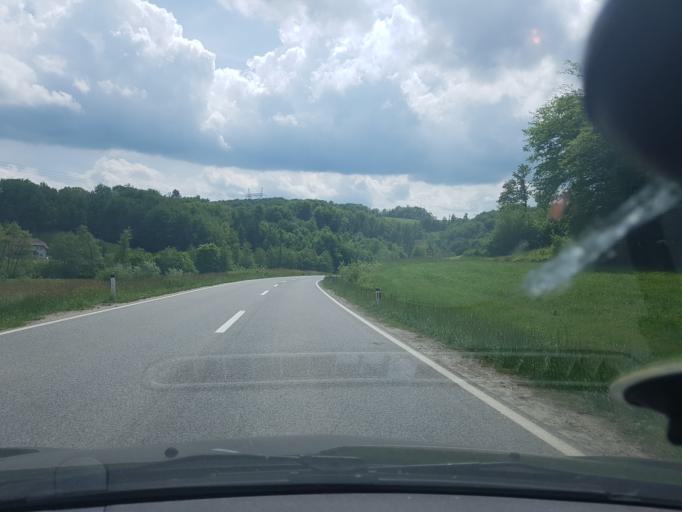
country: SI
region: Rogaska Slatina
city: Rogaska Slatina
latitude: 46.2446
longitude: 15.6055
